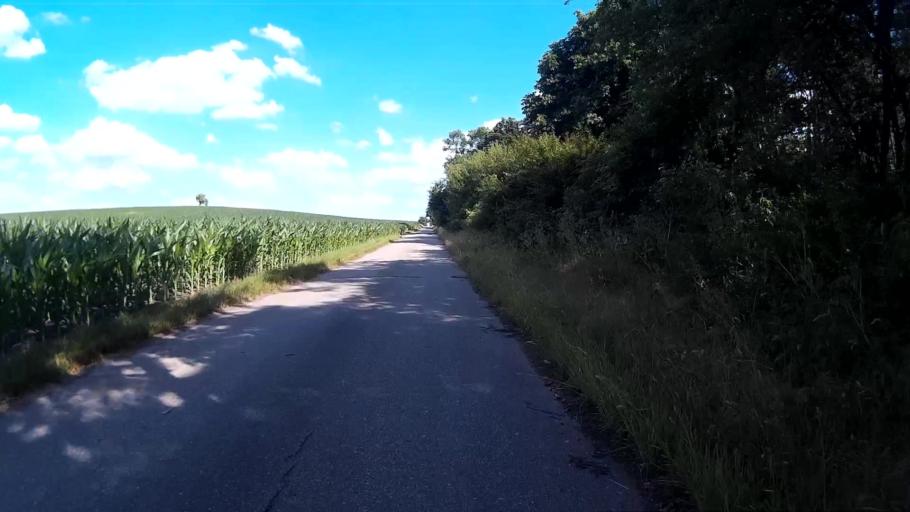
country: CZ
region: South Moravian
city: Moutnice
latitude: 49.0395
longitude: 16.7147
